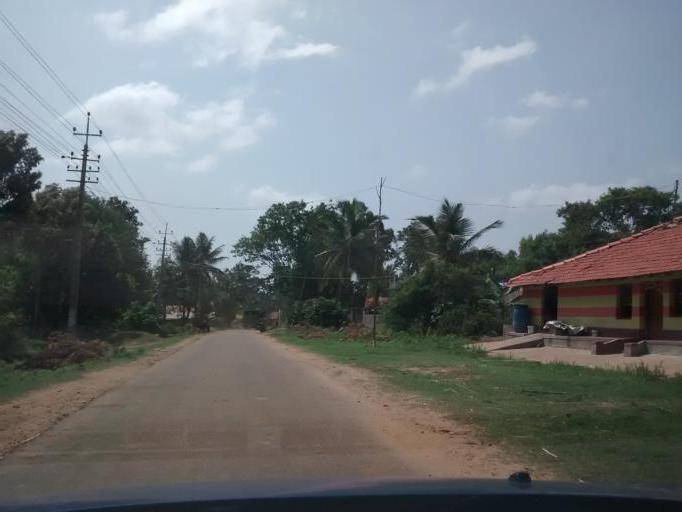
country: IN
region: Karnataka
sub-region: Hassan
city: Hole Narsipur
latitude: 12.7004
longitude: 76.1633
